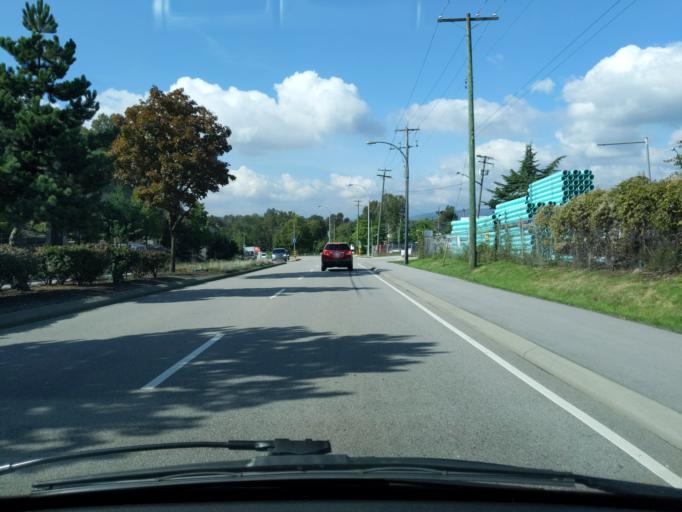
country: CA
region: British Columbia
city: New Westminster
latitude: 49.2058
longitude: -122.8555
